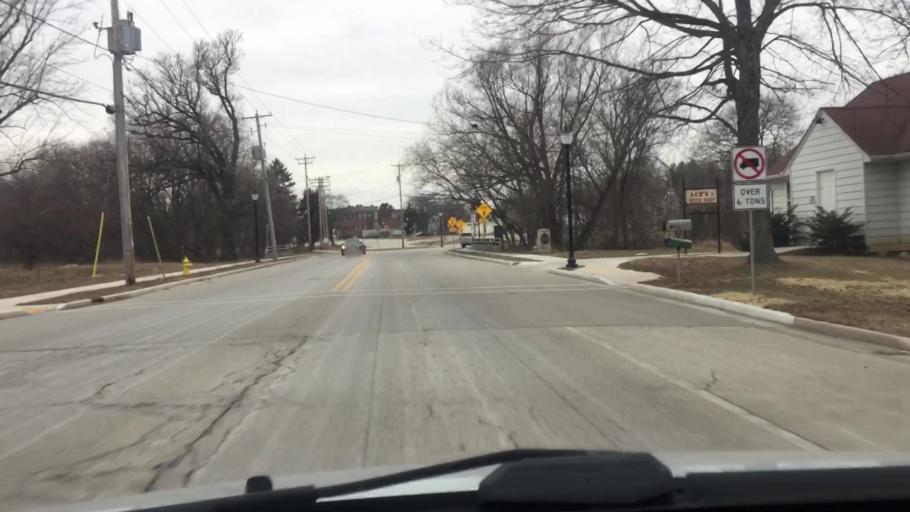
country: US
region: Wisconsin
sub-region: Waukesha County
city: Sussex
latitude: 43.1324
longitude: -88.2159
